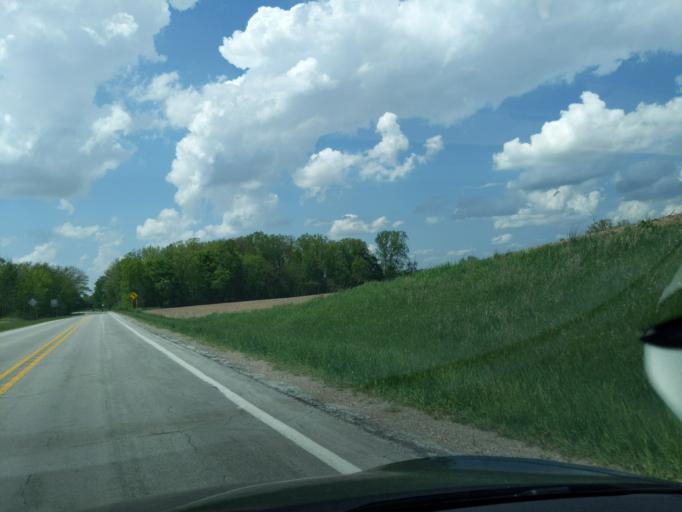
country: US
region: Michigan
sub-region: Ingham County
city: Stockbridge
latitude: 42.5533
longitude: -84.2328
